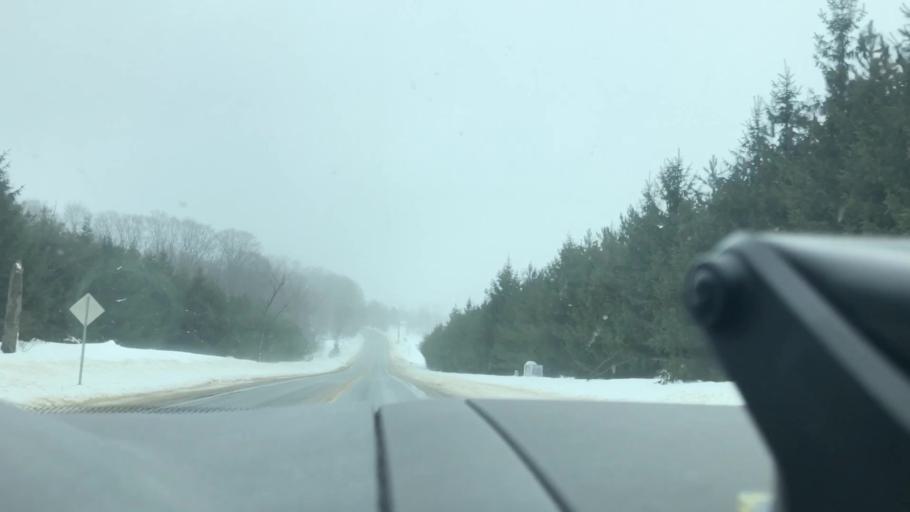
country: US
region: Michigan
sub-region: Charlevoix County
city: East Jordan
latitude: 45.1585
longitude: -85.1627
